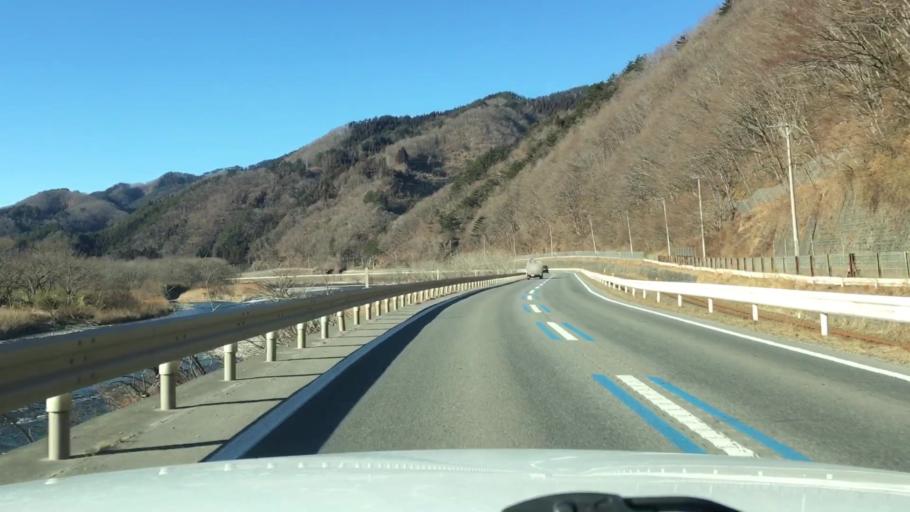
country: JP
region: Iwate
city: Miyako
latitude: 39.6308
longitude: 141.8541
